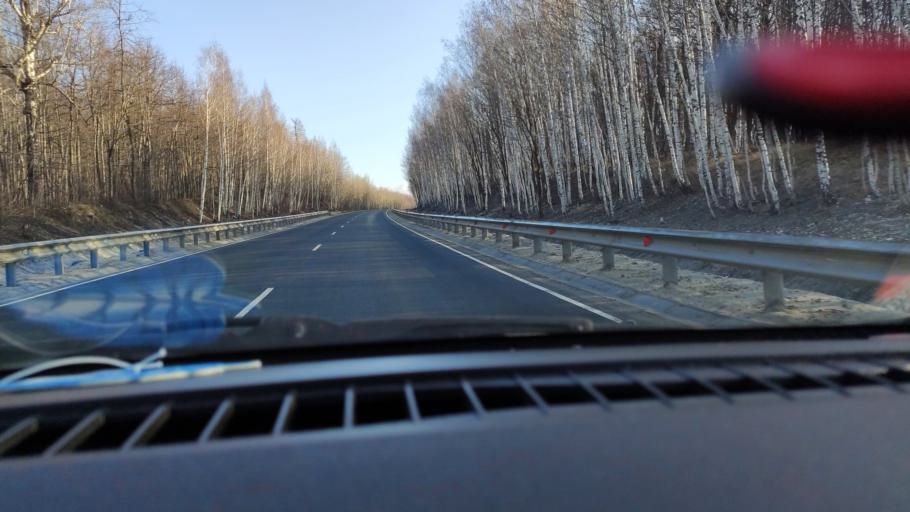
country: RU
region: Saratov
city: Khvalynsk
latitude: 52.4468
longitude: 48.0104
